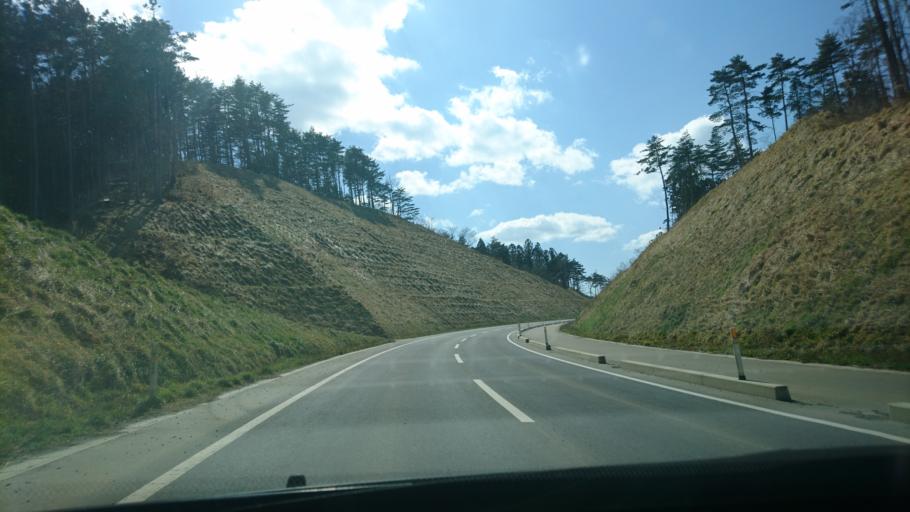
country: JP
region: Miyagi
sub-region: Oshika Gun
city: Onagawa Cho
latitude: 38.6387
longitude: 141.4485
